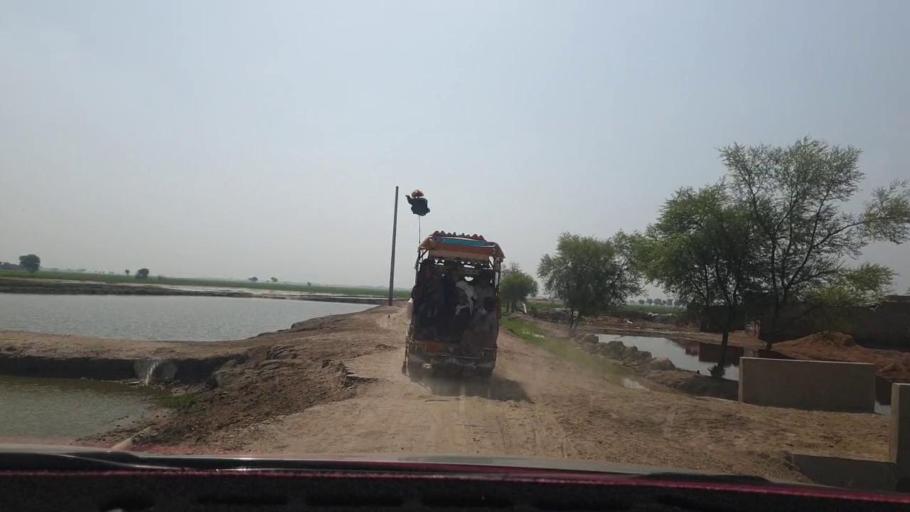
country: PK
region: Sindh
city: Warah
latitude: 27.4042
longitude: 67.8471
